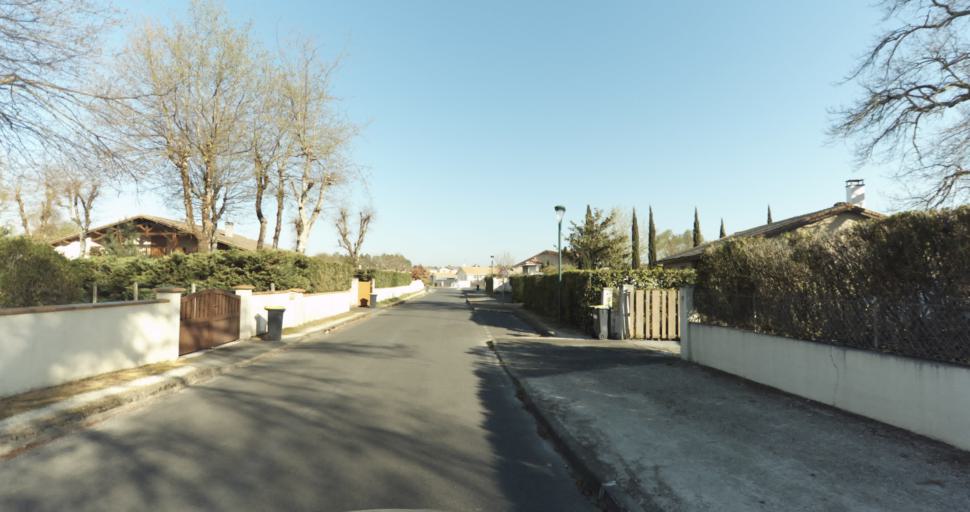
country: FR
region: Aquitaine
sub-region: Departement de la Gironde
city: Martignas-sur-Jalle
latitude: 44.8103
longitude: -0.7893
